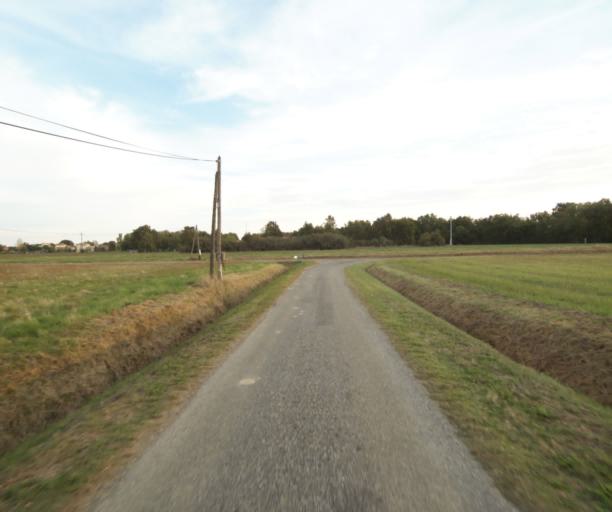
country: FR
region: Midi-Pyrenees
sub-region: Departement du Tarn-et-Garonne
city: Pompignan
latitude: 43.8203
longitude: 1.3228
